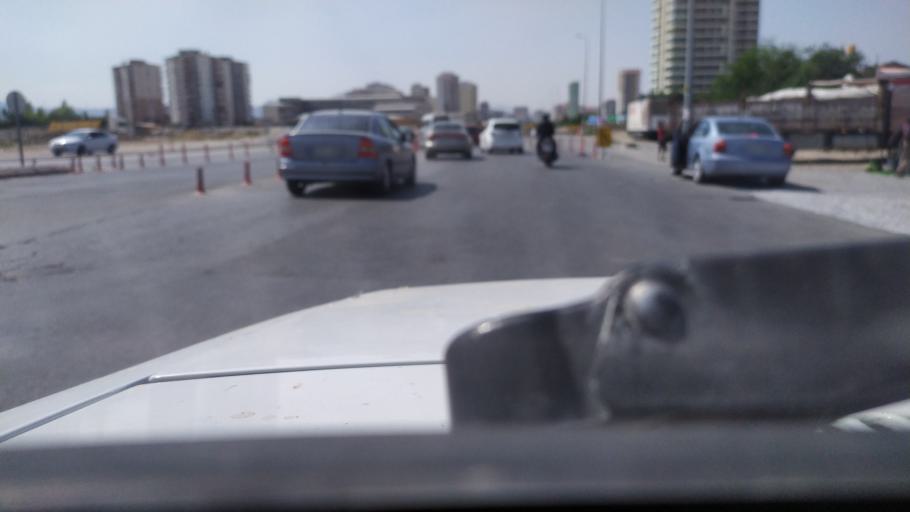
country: TR
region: Kayseri
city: Talas
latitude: 38.7199
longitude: 35.5505
